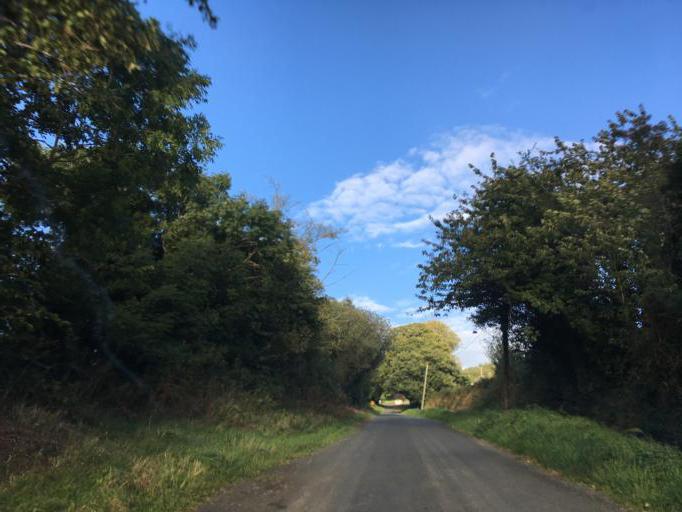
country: IE
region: Leinster
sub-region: Wicklow
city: Wicklow
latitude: 52.9165
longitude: -6.0834
